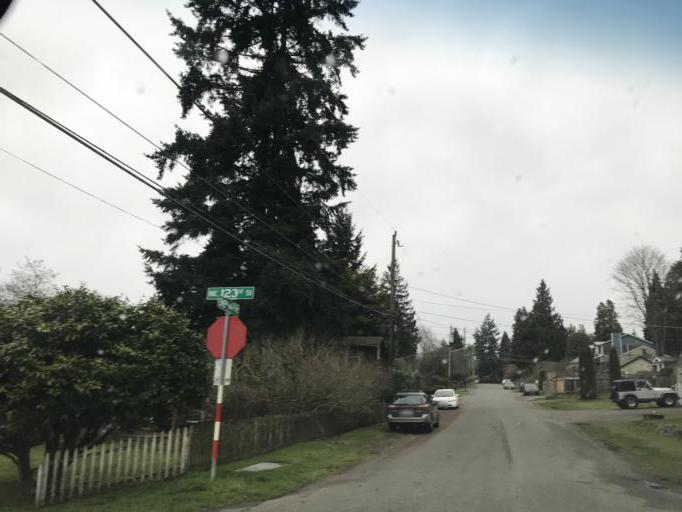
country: US
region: Washington
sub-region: King County
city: Lake Forest Park
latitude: 47.7173
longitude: -122.2893
